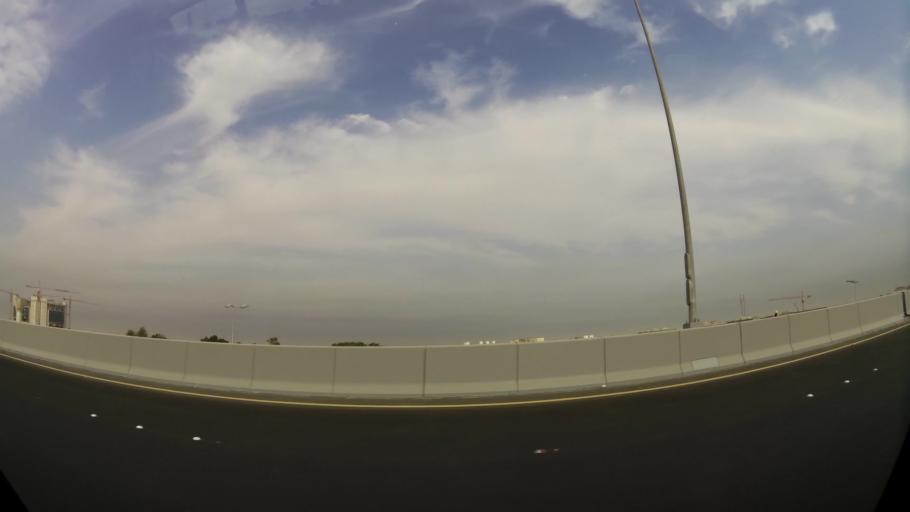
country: KW
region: Al Asimah
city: Ar Rabiyah
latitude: 29.3237
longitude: 47.8907
